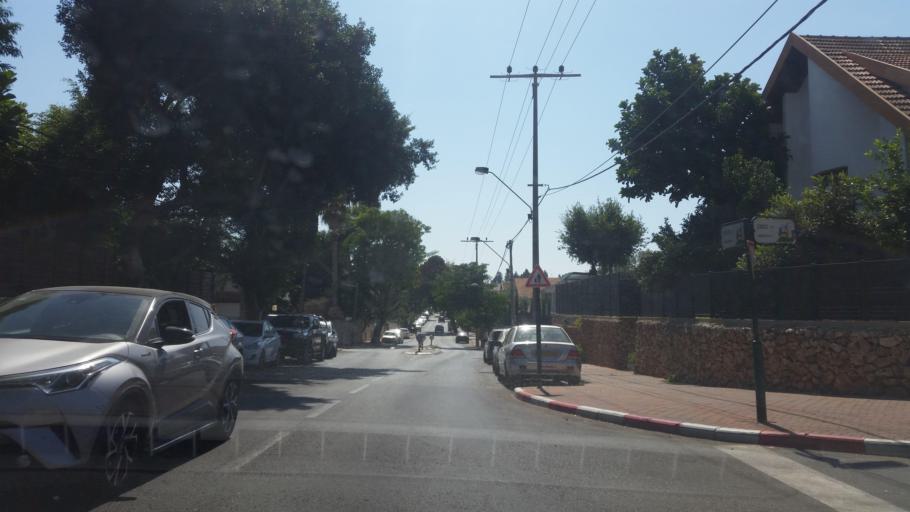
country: IL
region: Central District
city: Ra'anana
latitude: 32.1843
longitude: 34.8862
